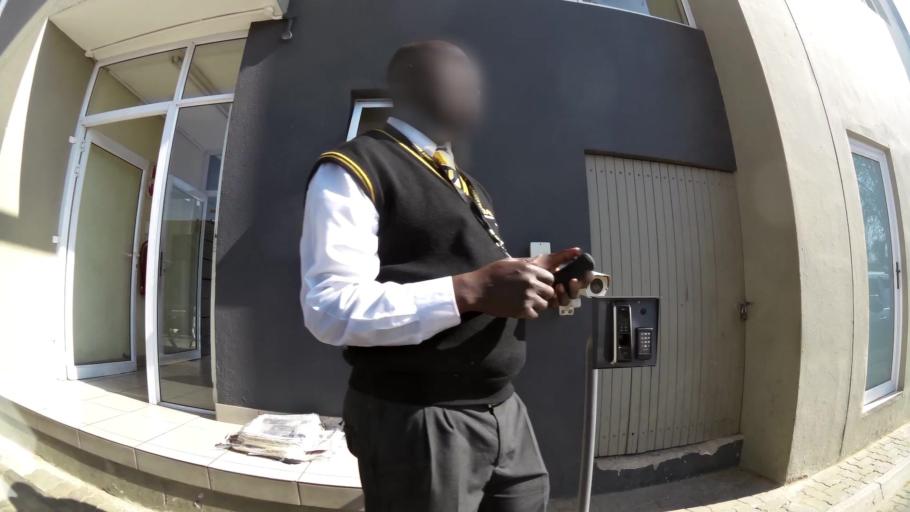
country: ZA
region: Gauteng
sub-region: City of Johannesburg Metropolitan Municipality
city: Modderfontein
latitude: -26.1187
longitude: 28.1522
